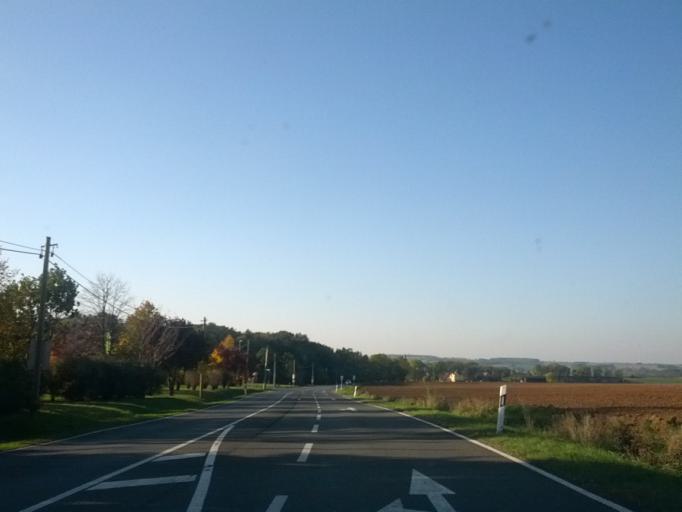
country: DE
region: Thuringia
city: Schwaara
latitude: 50.8876
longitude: 12.1390
